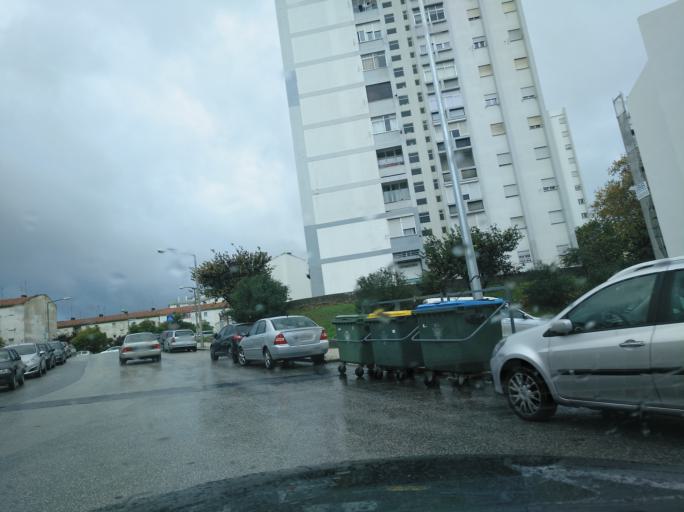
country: PT
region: Lisbon
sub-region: Loures
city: Moscavide
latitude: 38.7608
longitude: -9.1094
